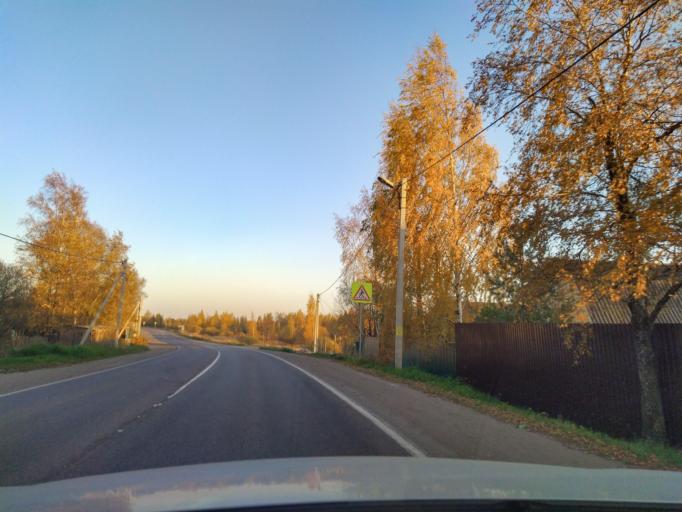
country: RU
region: Leningrad
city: Maloye Verevo
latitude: 59.6126
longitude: 30.2228
